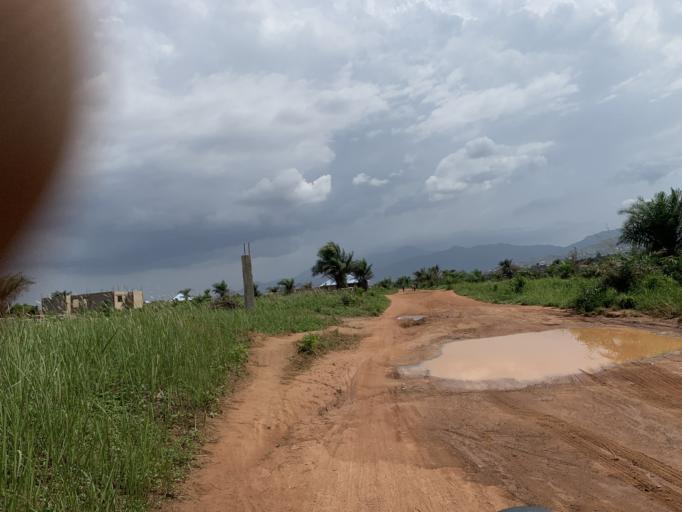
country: SL
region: Western Area
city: Waterloo
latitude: 8.3589
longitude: -13.0465
